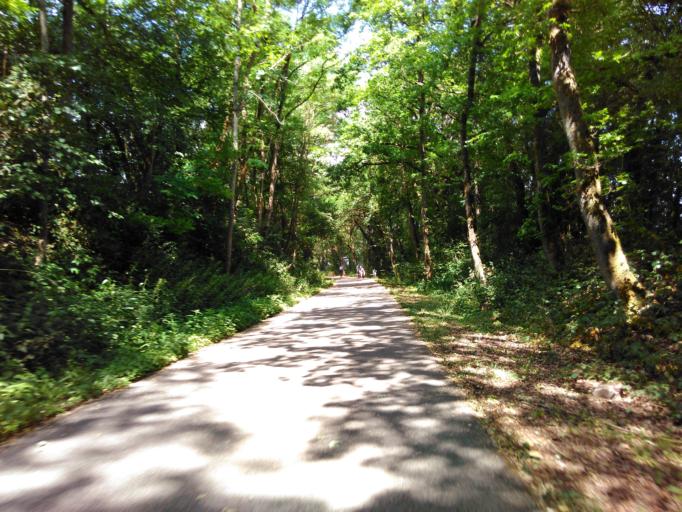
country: LU
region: Luxembourg
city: Hautcharage
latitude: 49.5853
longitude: 5.9090
